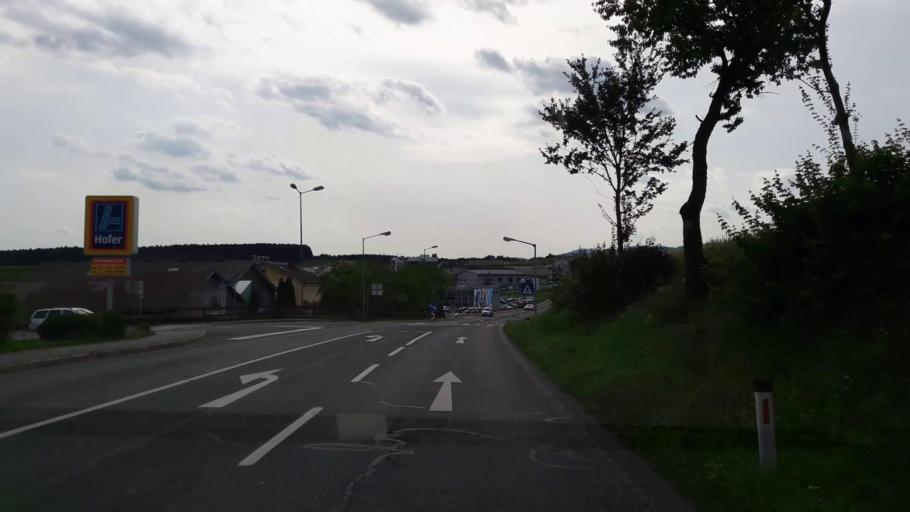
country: AT
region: Styria
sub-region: Politischer Bezirk Hartberg-Fuerstenfeld
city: Hartberg
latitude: 47.2720
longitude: 15.9611
